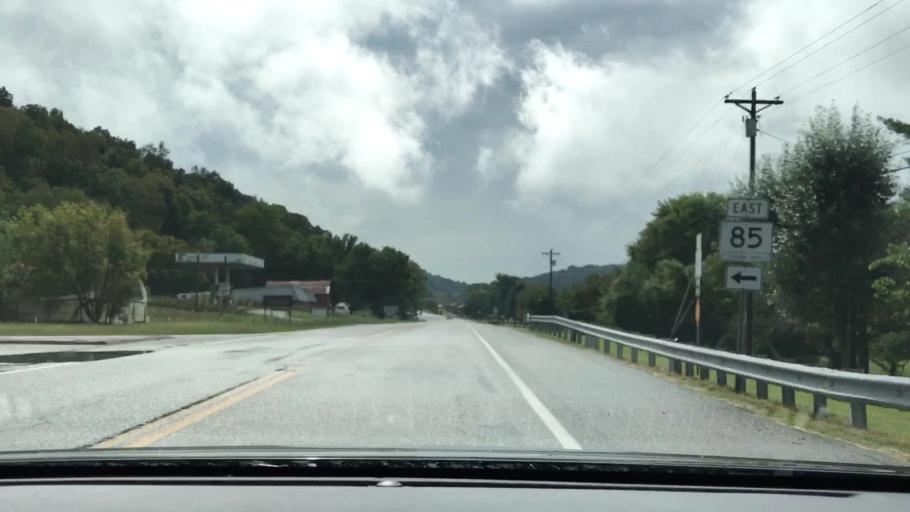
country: US
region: Tennessee
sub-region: Smith County
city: Carthage
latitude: 36.3187
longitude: -85.9690
